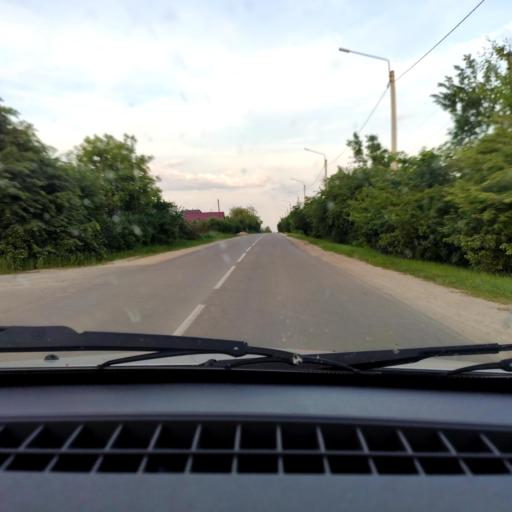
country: RU
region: Voronezj
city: Ramon'
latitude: 51.9526
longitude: 39.3622
